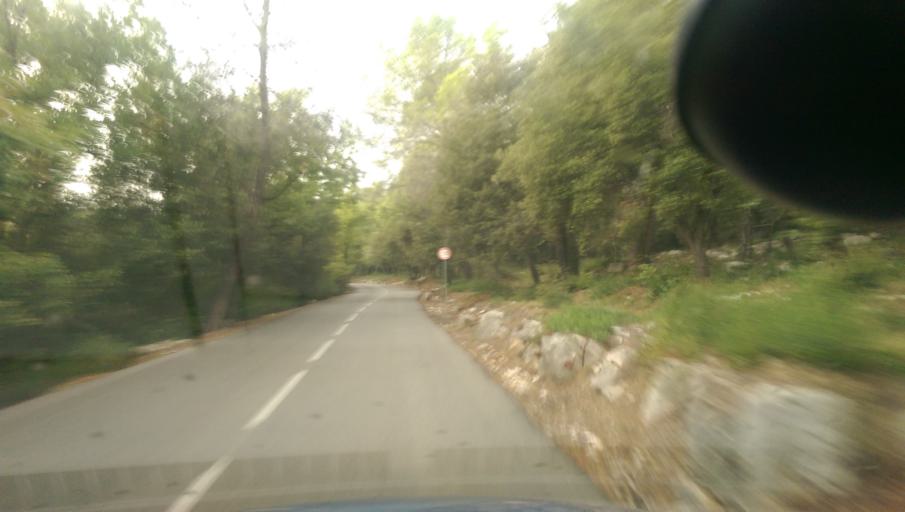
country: FR
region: Provence-Alpes-Cote d'Azur
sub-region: Departement des Alpes-Maritimes
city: Valbonne
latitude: 43.6391
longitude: 7.0440
